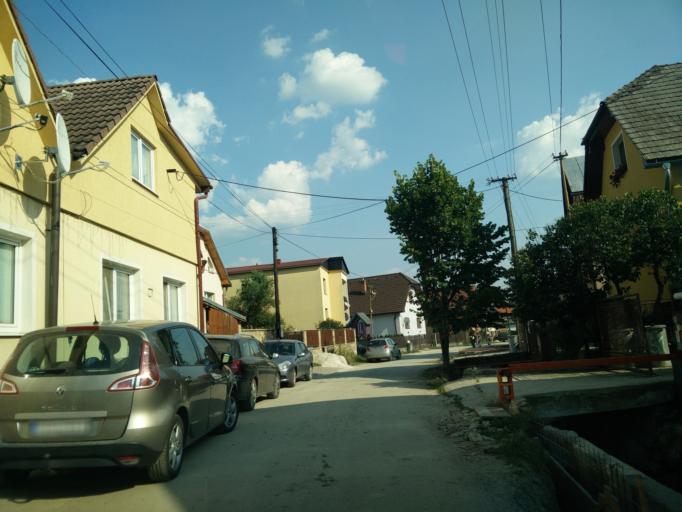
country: SK
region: Zilinsky
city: Rajec
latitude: 49.1225
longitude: 18.6453
